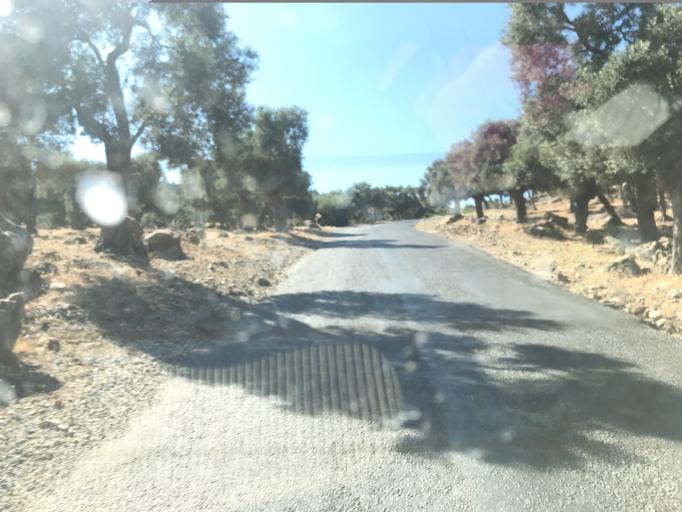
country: TR
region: Mugla
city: Selimiye
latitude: 37.3826
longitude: 27.4850
